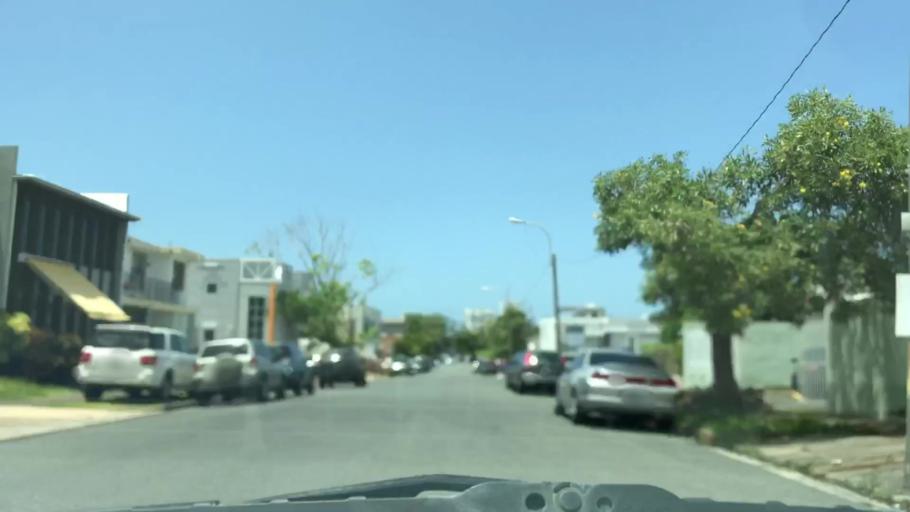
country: PR
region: Catano
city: Catano
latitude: 18.4157
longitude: -66.0619
